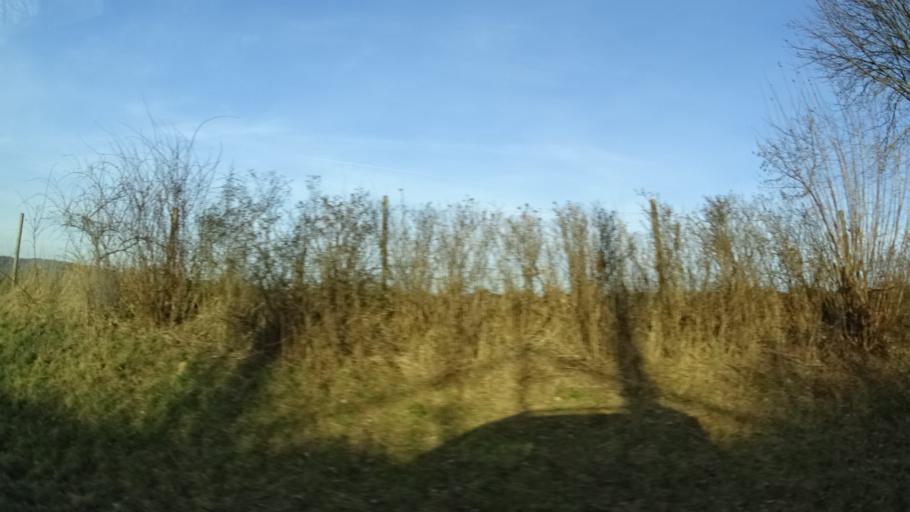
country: DE
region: Hesse
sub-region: Regierungsbezirk Darmstadt
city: Schluchtern
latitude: 50.3389
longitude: 9.5686
